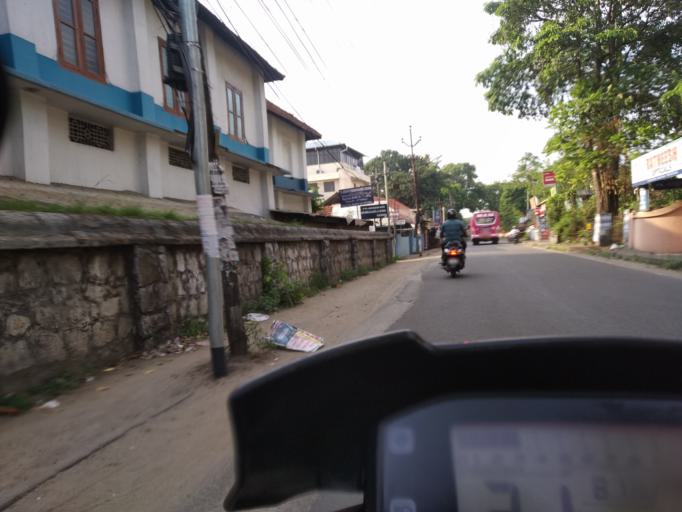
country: IN
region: Kerala
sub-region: Ernakulam
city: Cochin
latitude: 9.9534
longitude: 76.3453
